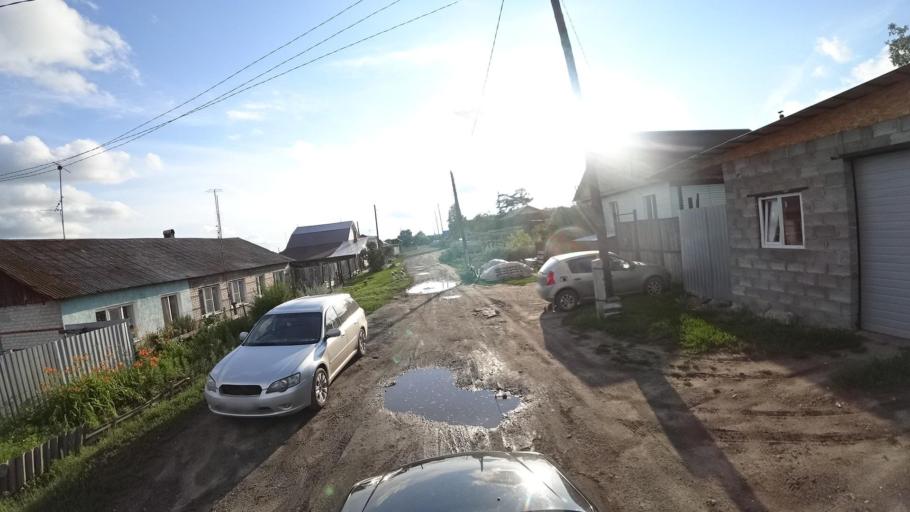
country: RU
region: Sverdlovsk
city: Kamyshlov
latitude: 56.8483
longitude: 62.6679
